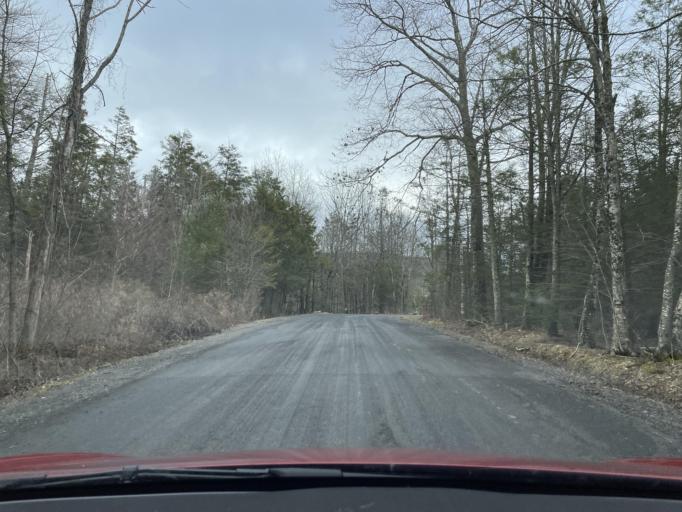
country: US
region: New York
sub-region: Ulster County
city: Woodstock
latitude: 42.0753
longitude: -74.1269
